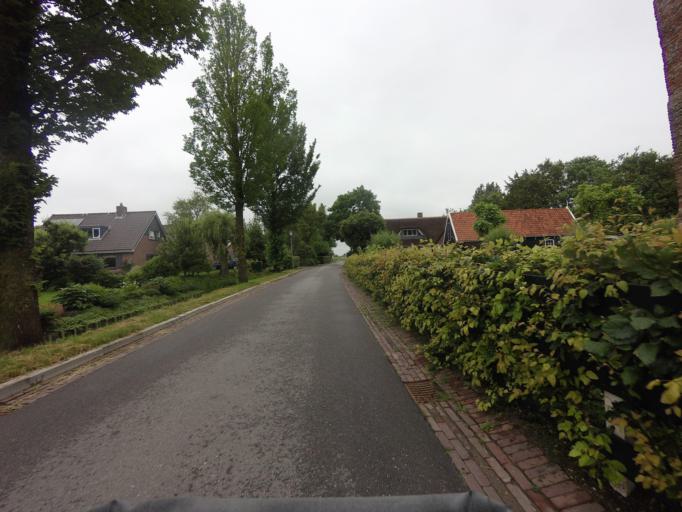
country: NL
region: North Holland
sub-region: Gemeente Schagen
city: Schagen
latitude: 52.7744
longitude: 4.8283
